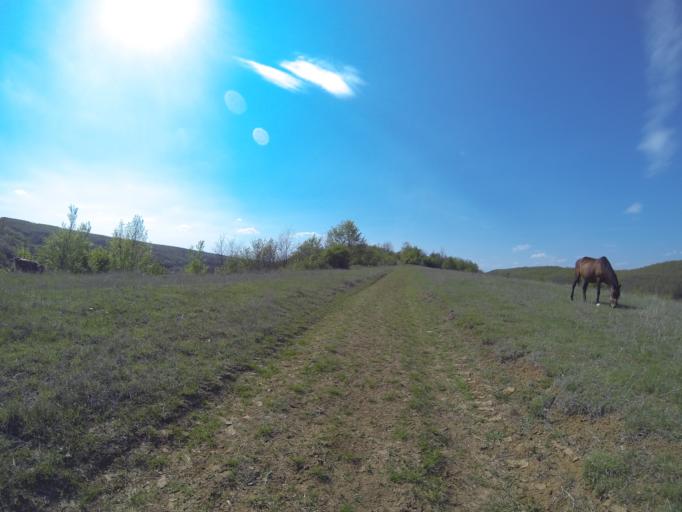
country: RO
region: Gorj
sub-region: Comuna Crusetu
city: Crusetu
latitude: 44.6201
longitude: 23.6553
